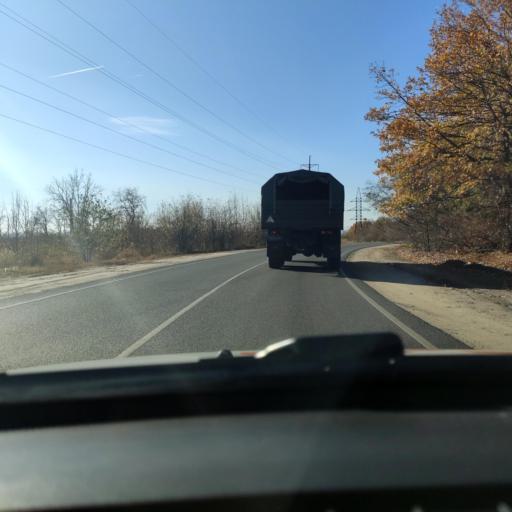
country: RU
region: Voronezj
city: Shilovo
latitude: 51.5614
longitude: 39.1400
